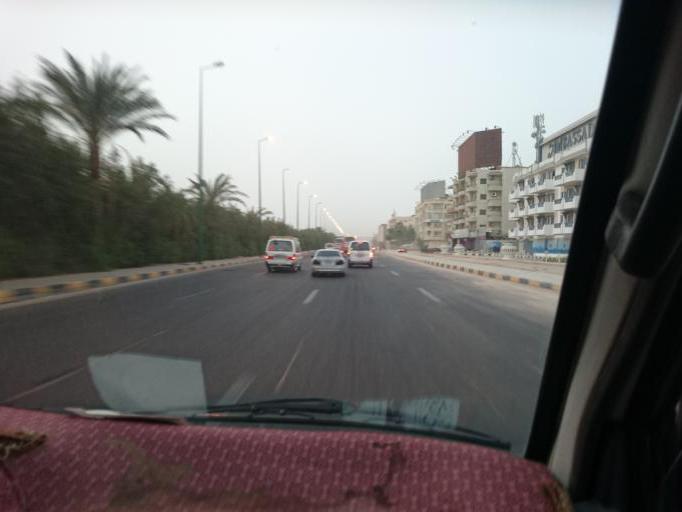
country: EG
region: Red Sea
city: Hurghada
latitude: 27.1893
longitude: 33.8218
